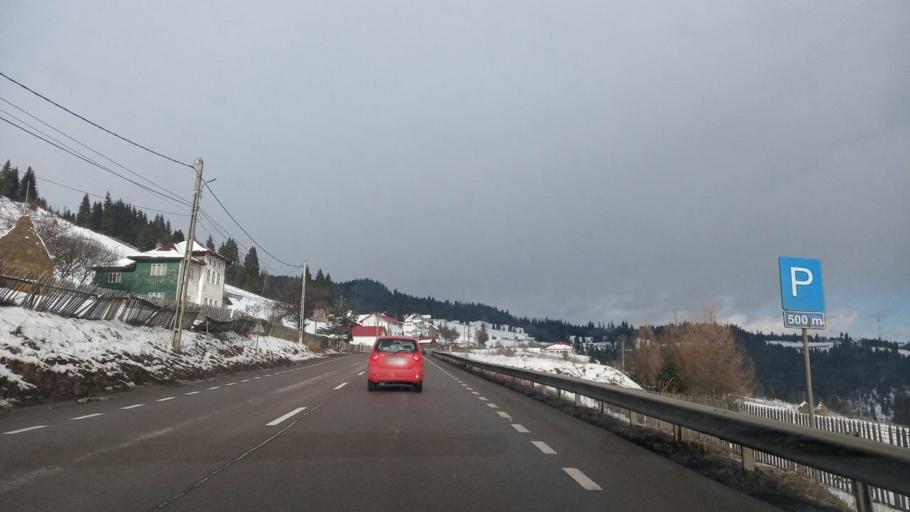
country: RO
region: Suceava
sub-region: Comuna Iacobeni
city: Iacobeni
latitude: 47.4558
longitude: 25.3304
